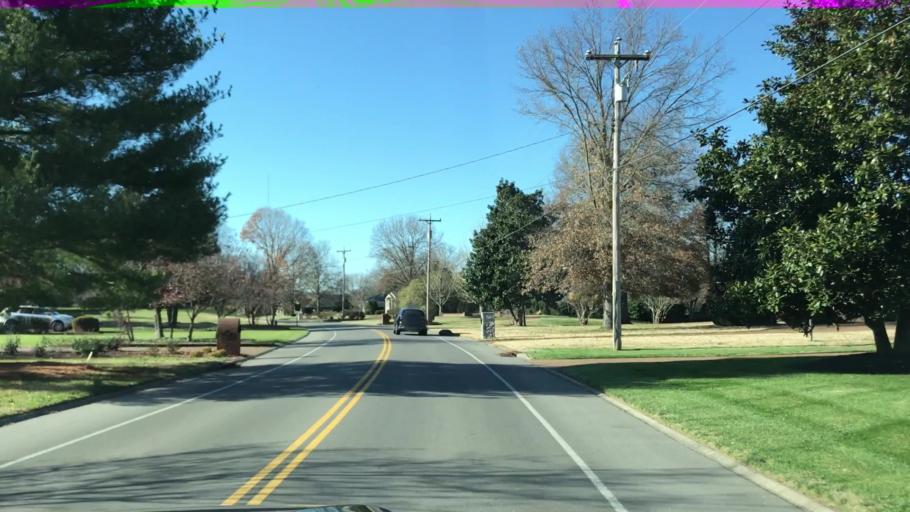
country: US
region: Tennessee
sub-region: Williamson County
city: Brentwood
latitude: 36.0252
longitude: -86.8219
